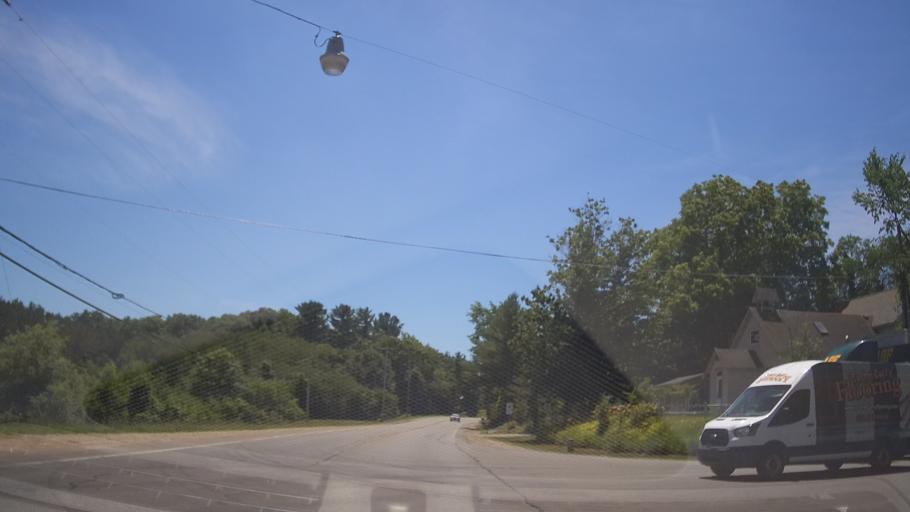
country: US
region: Michigan
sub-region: Grand Traverse County
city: Traverse City
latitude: 44.7160
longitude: -85.6855
